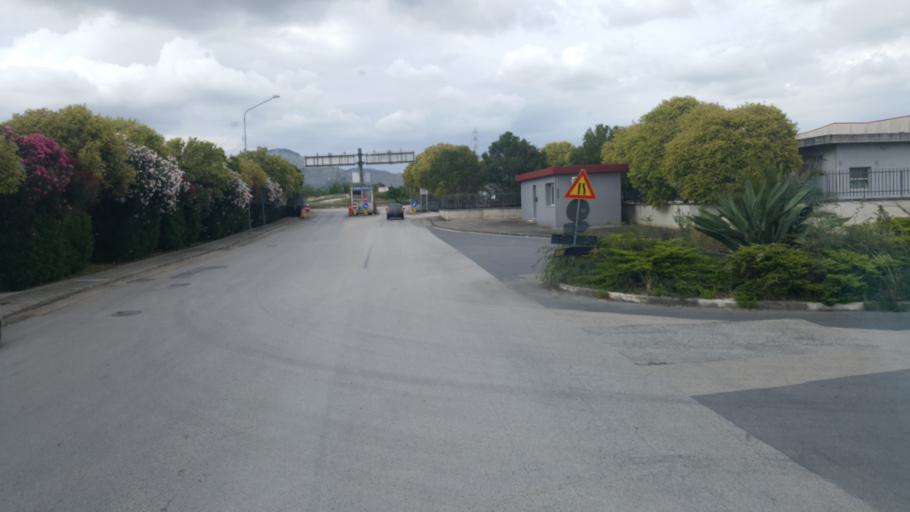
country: IT
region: Campania
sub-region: Provincia di Caserta
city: Maddaloni
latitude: 41.0107
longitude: 14.3684
